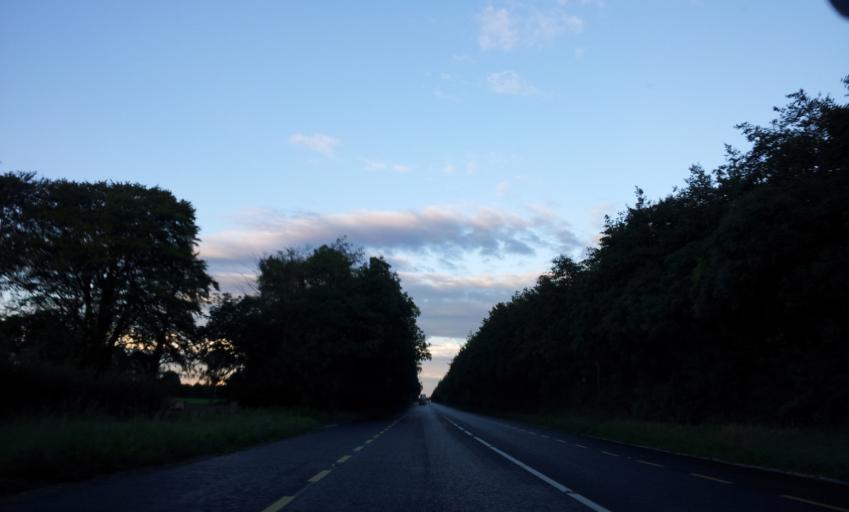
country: IE
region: Munster
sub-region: County Limerick
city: Rathkeale
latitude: 52.5129
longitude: -8.9808
